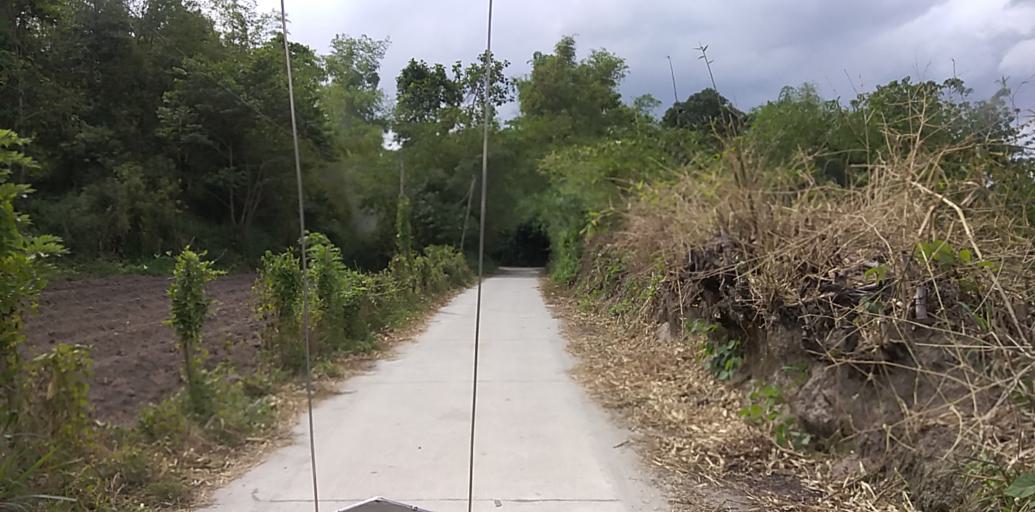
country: PH
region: Central Luzon
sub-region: Province of Pampanga
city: Porac
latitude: 15.0580
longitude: 120.5332
